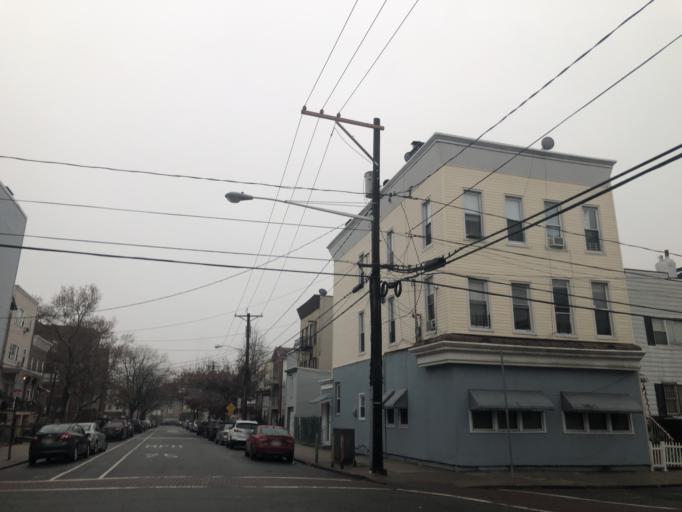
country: US
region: New Jersey
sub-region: Hudson County
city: Hoboken
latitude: 40.7442
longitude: -74.0483
